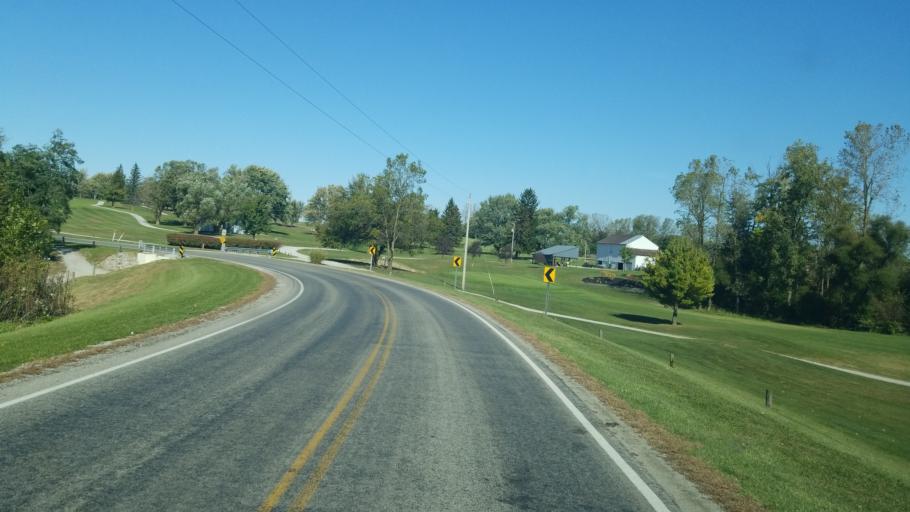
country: US
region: Ohio
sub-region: Hardin County
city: Kenton
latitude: 40.6378
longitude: -83.5743
